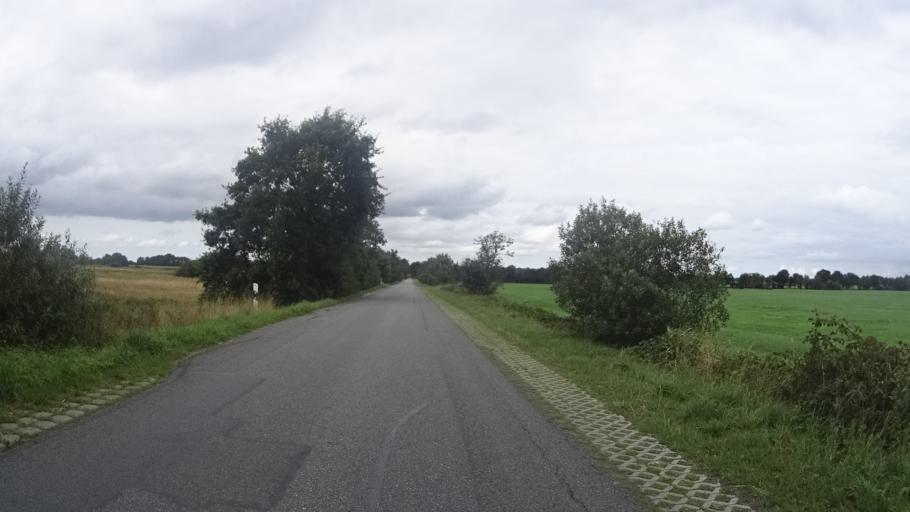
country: DE
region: Lower Saxony
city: Stinstedt
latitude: 53.6469
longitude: 8.9618
